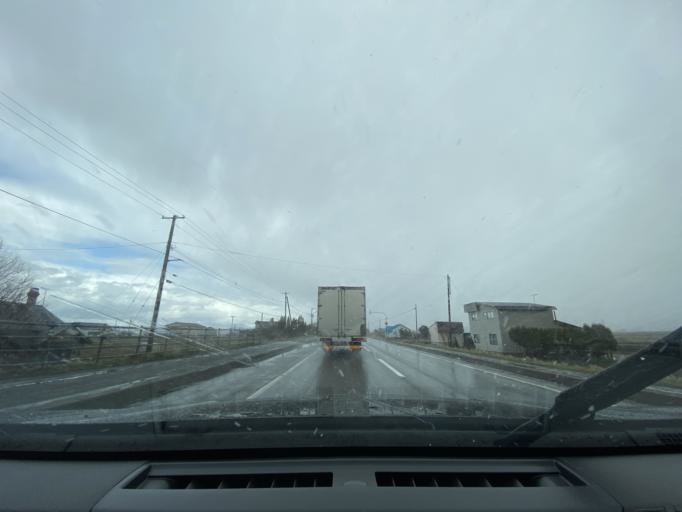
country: JP
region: Hokkaido
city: Fukagawa
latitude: 43.6573
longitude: 141.9841
